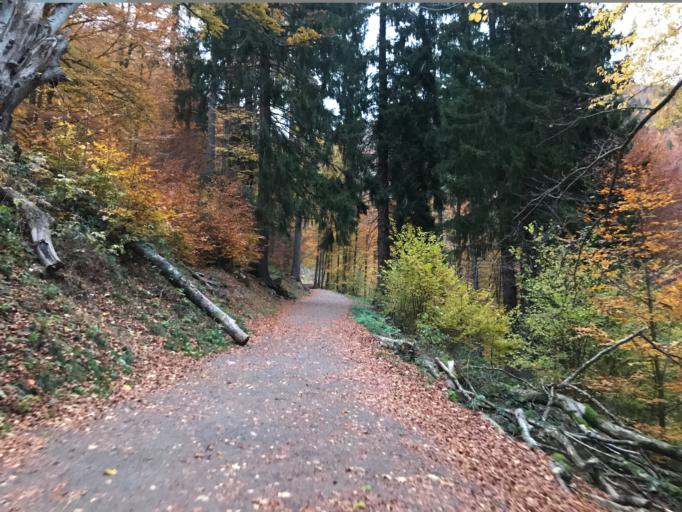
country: DE
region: Baden-Wuerttemberg
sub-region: Freiburg Region
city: Todtnau
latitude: 47.8420
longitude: 7.9366
